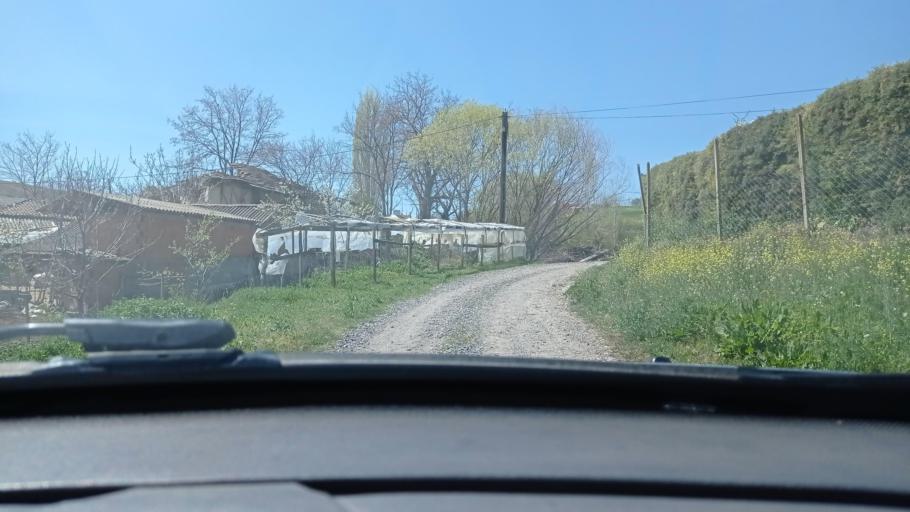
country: MK
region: Lozovo
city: Lozovo
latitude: 41.8043
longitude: 21.8655
